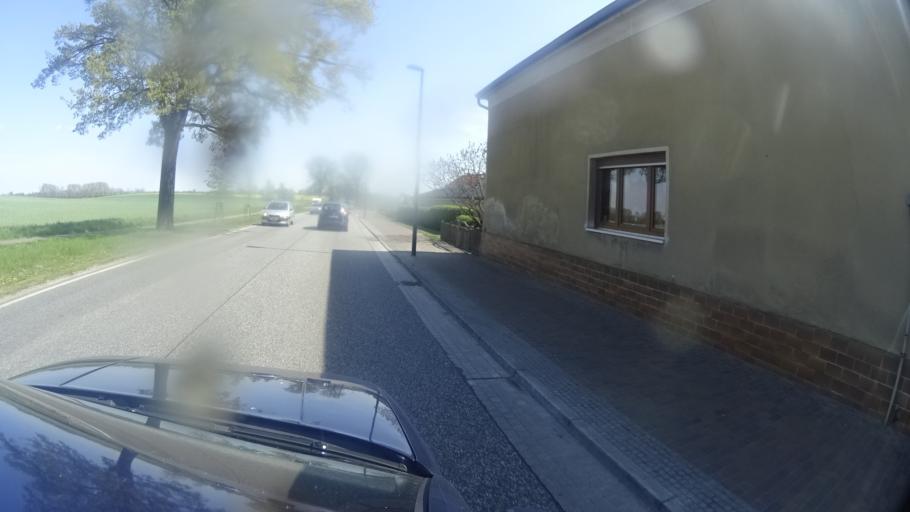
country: DE
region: Brandenburg
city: Nauen
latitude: 52.6201
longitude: 12.8016
